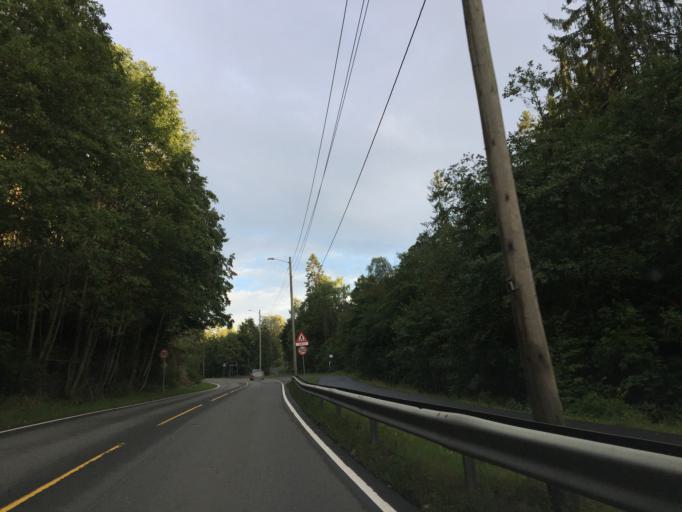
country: NO
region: Akershus
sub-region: Oppegard
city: Kolbotn
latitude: 59.8410
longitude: 10.8270
